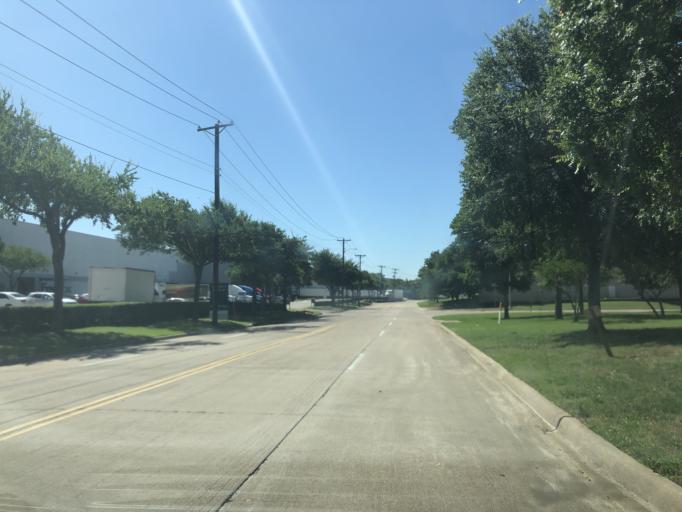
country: US
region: Texas
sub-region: Tarrant County
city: Euless
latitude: 32.7986
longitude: -97.0414
